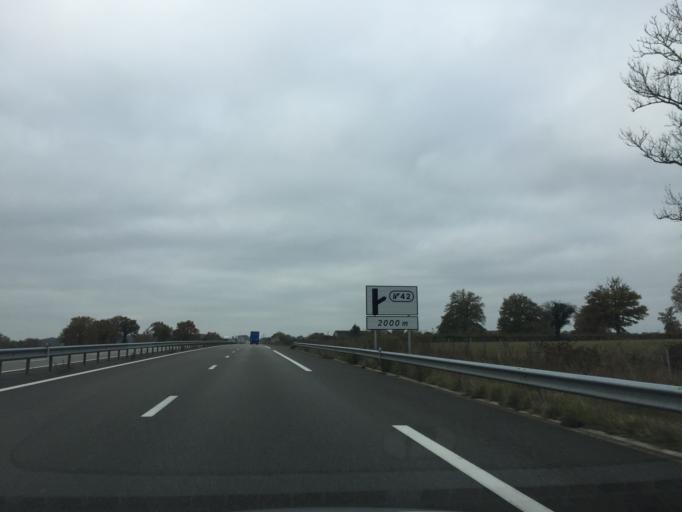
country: FR
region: Limousin
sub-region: Departement de la Creuse
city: Chambon-sur-Voueize
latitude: 46.2735
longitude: 2.3840
